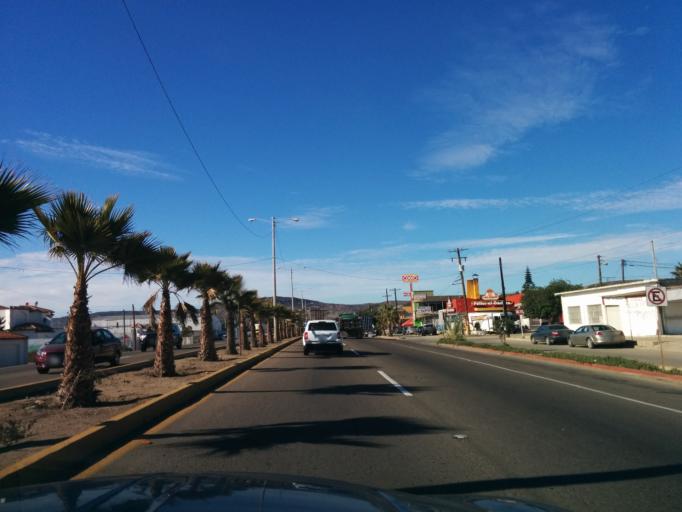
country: MX
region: Baja California
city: El Sauzal
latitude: 31.8944
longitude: -116.6973
